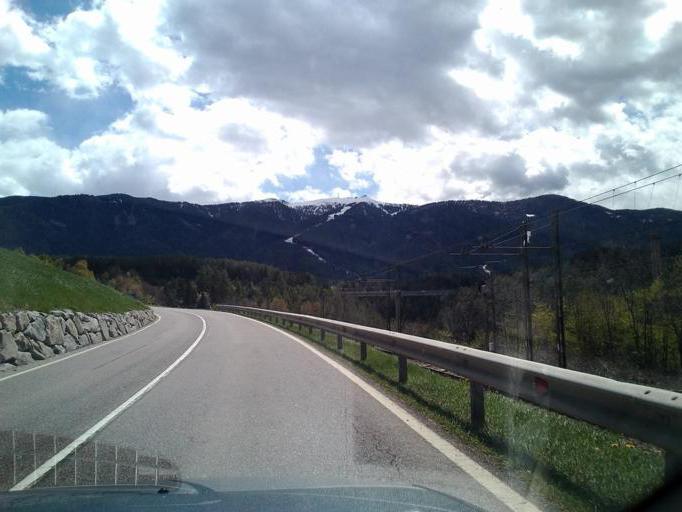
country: IT
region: Trentino-Alto Adige
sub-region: Bolzano
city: Riscone
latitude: 46.7936
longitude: 11.9516
